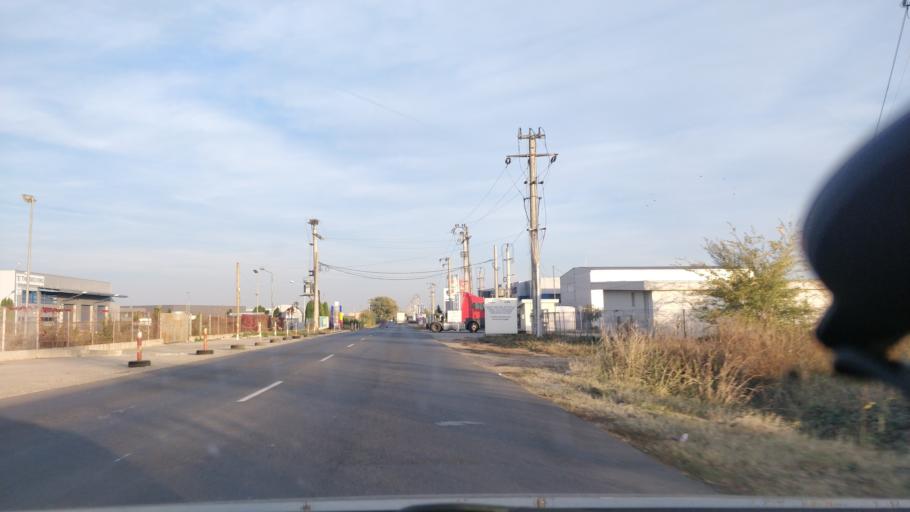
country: RO
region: Ilfov
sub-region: Comuna Dragomiresti-Vale
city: Dragomiresti-Deal
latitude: 44.4399
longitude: 25.9243
